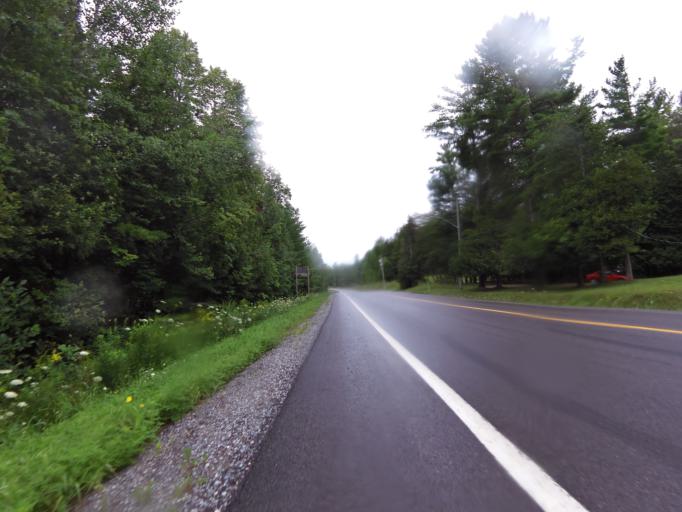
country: CA
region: Ontario
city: Perth
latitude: 45.0095
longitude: -76.3696
